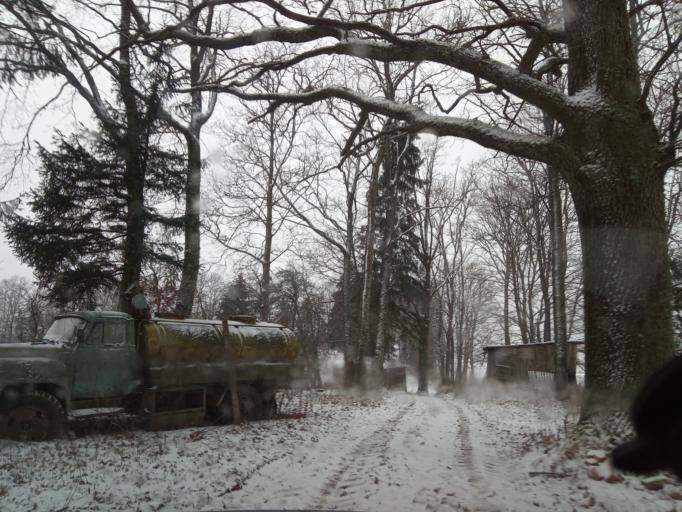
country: LT
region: Utenos apskritis
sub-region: Anyksciai
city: Anyksciai
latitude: 55.4057
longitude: 25.1743
